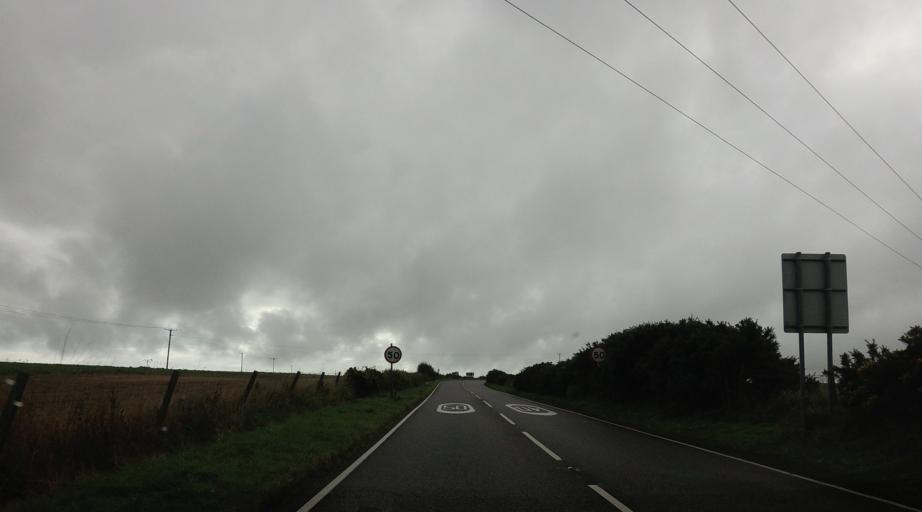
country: GB
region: Scotland
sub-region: Fife
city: Balmullo
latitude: 56.4092
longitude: -2.9138
